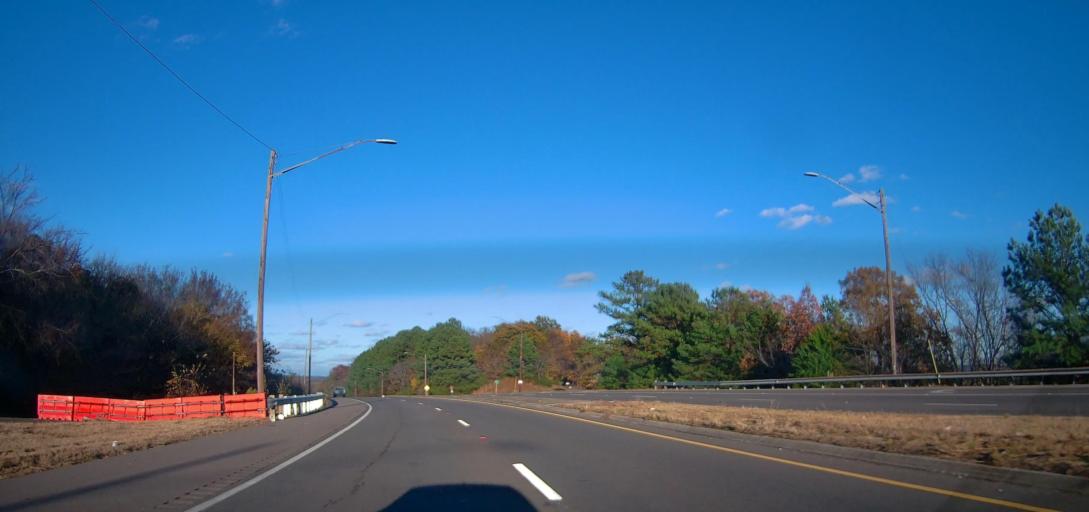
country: US
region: Alabama
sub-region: Jefferson County
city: Fultondale
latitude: 33.5650
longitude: -86.8171
